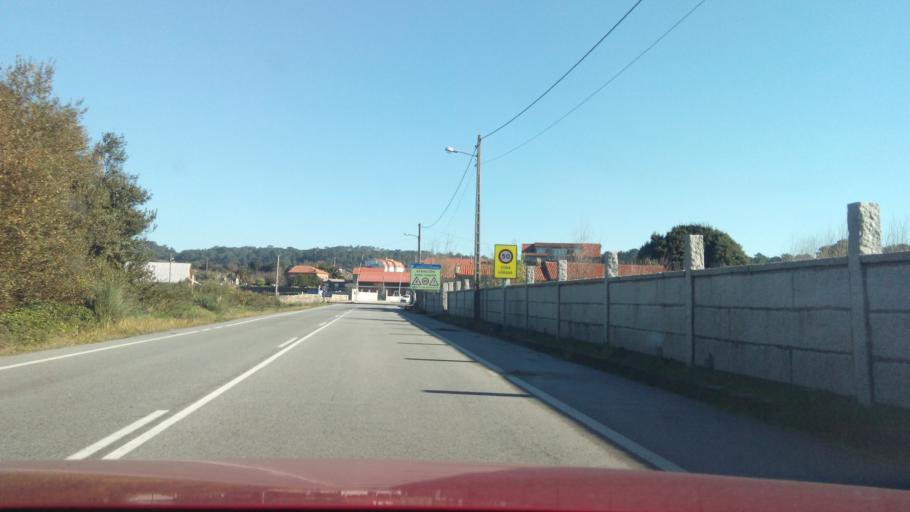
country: ES
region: Galicia
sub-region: Provincia de Pontevedra
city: O Grove
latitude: 42.4685
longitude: -8.9094
